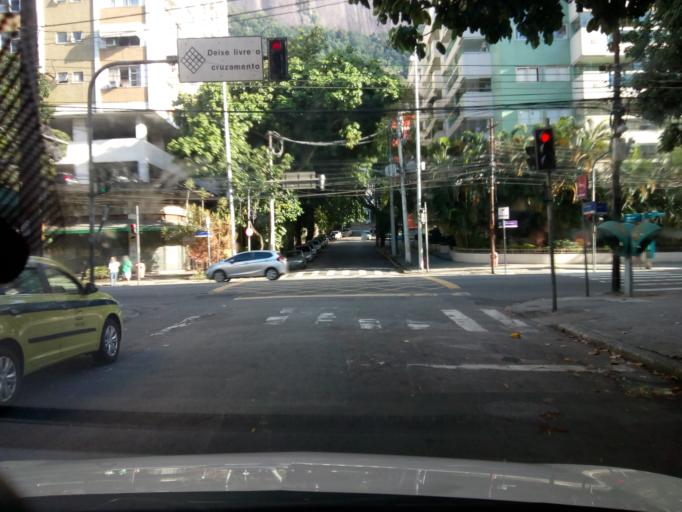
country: BR
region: Rio de Janeiro
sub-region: Rio De Janeiro
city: Rio de Janeiro
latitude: -22.9610
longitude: -43.2079
